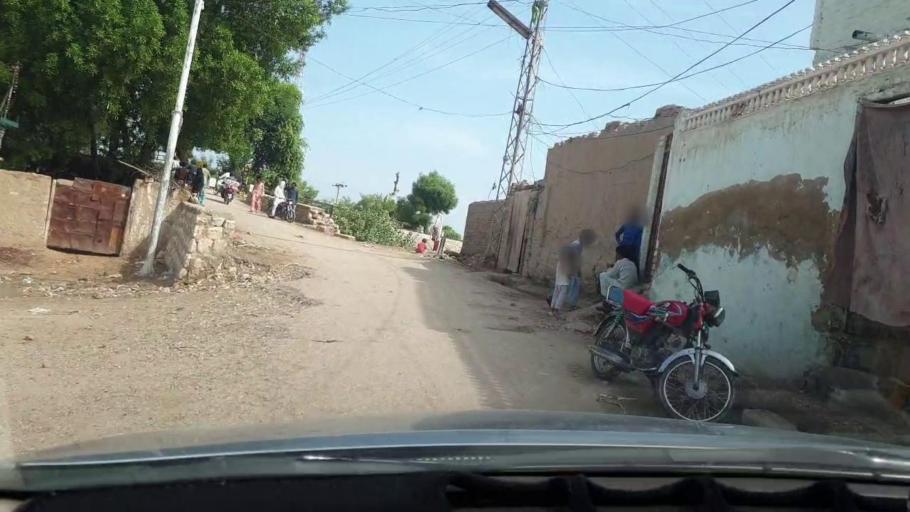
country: PK
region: Sindh
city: Khairpur
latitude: 27.5371
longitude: 68.7516
